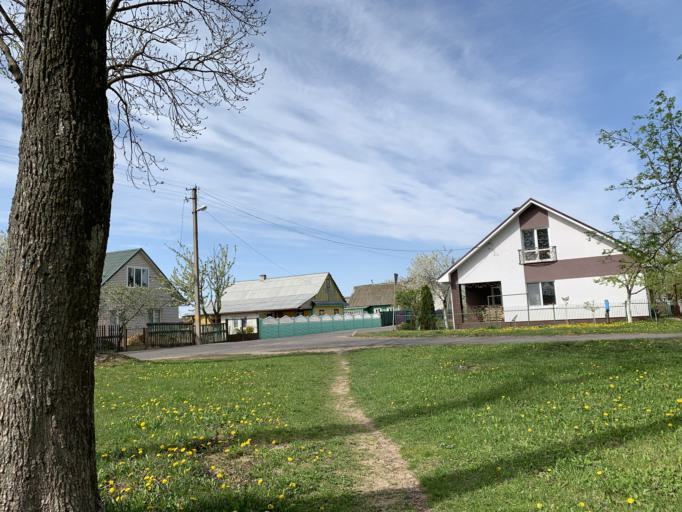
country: BY
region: Minsk
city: Nyasvizh
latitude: 53.2179
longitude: 26.6711
